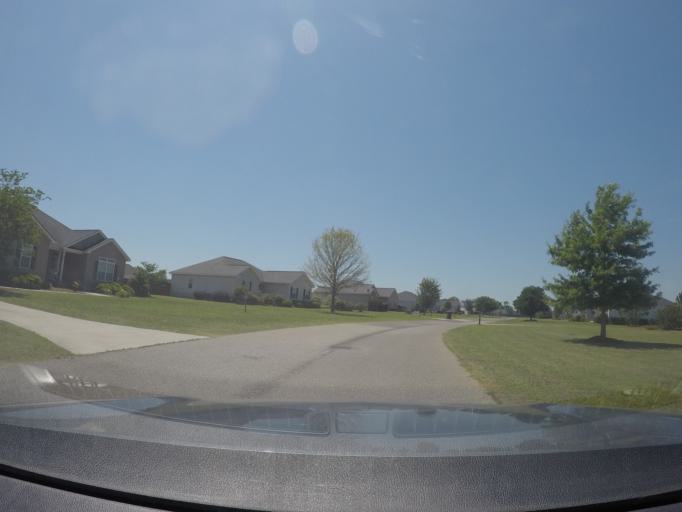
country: US
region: Georgia
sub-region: Bulloch County
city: Brooklet
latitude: 32.3589
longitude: -81.7541
